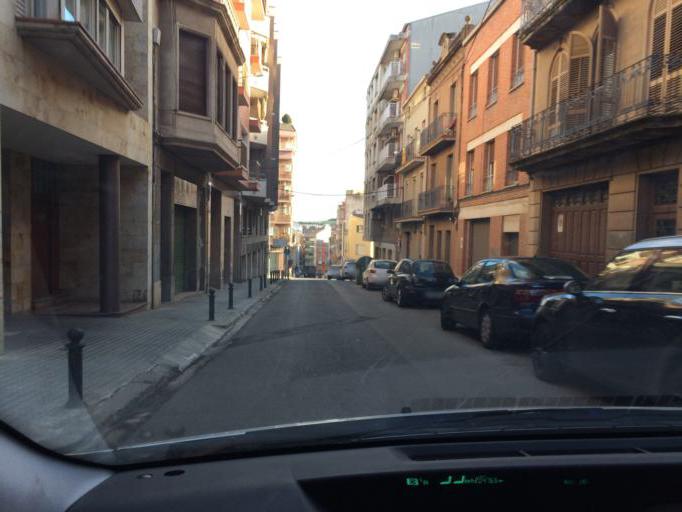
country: ES
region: Catalonia
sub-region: Provincia de Barcelona
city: Manresa
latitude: 41.7273
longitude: 1.8201
